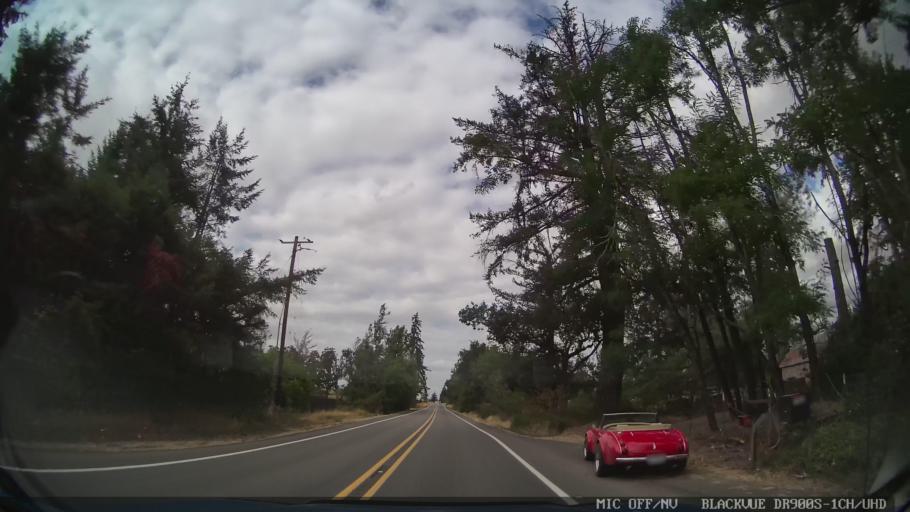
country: US
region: Oregon
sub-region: Marion County
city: Sublimity
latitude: 44.8511
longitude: -122.7934
